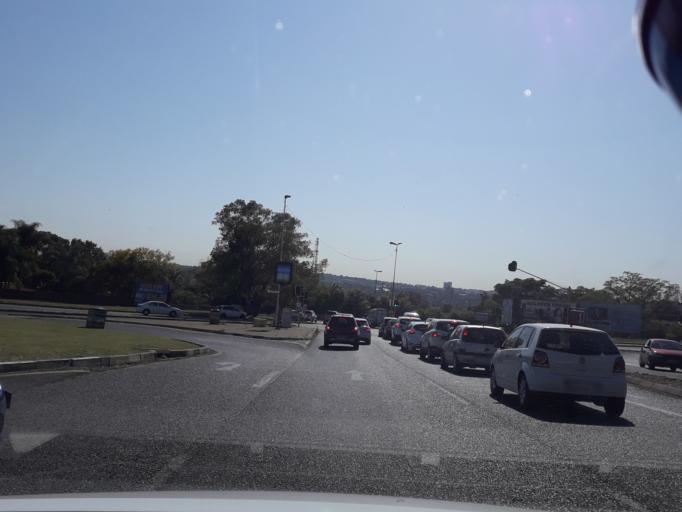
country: ZA
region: Gauteng
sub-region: City of Johannesburg Metropolitan Municipality
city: Roodepoort
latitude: -26.0919
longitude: 27.9593
